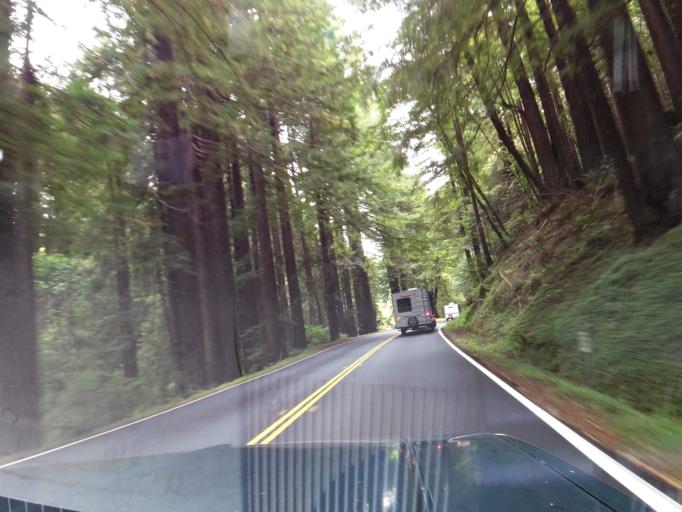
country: US
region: California
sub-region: Mendocino County
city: Fort Bragg
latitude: 39.1795
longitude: -123.7098
